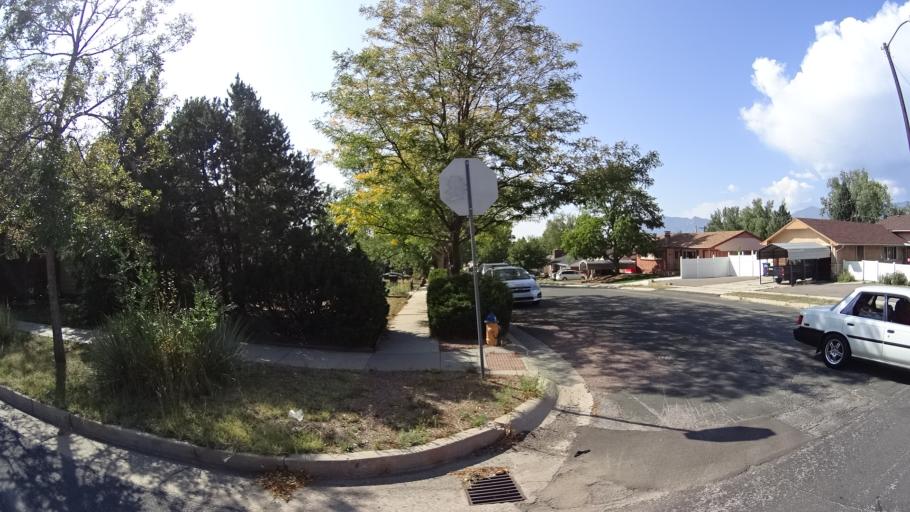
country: US
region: Colorado
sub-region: El Paso County
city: Colorado Springs
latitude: 38.8651
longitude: -104.7702
